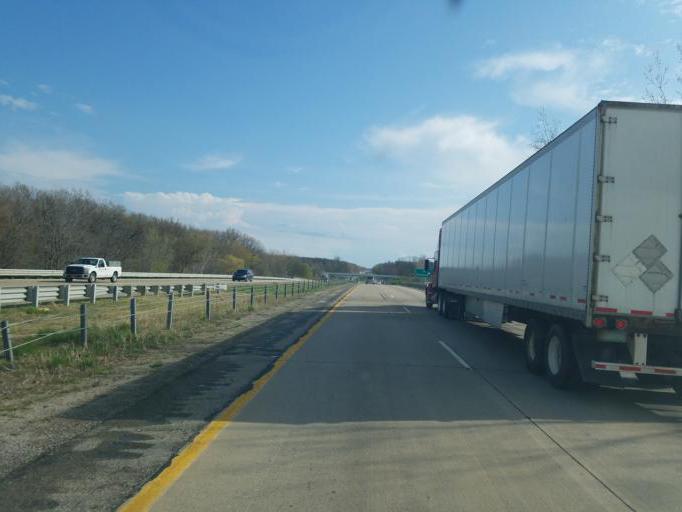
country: US
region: Michigan
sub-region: Monroe County
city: Dundee
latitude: 41.9139
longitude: -83.6621
